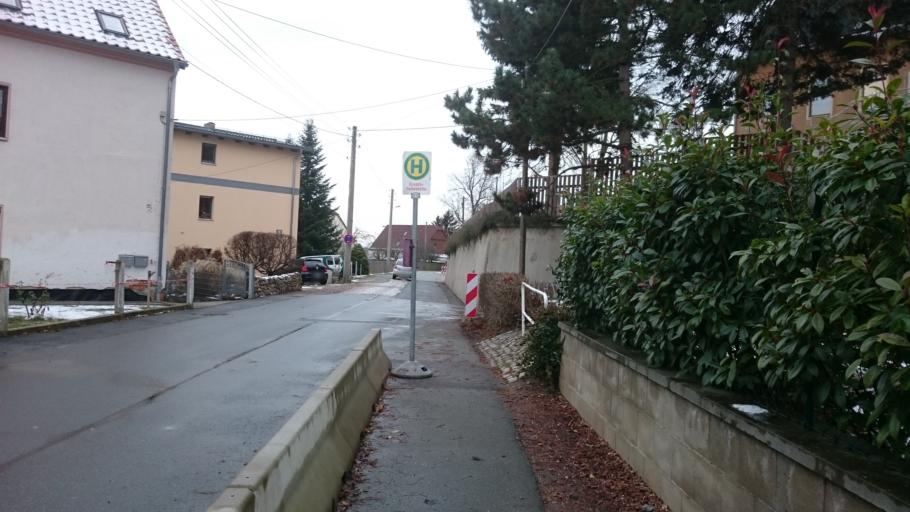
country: DE
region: Saxony
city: Pfaffroda
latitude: 50.8311
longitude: 12.5139
